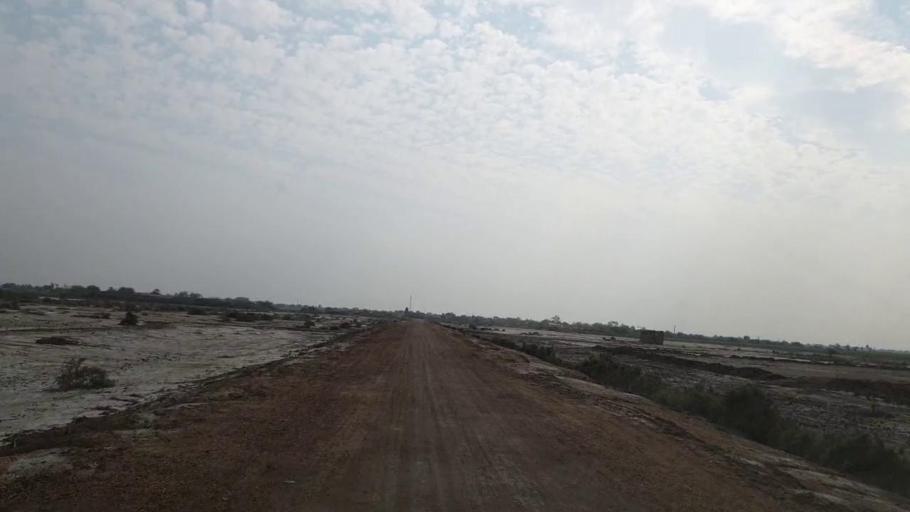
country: PK
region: Sindh
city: Mirpur Khas
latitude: 25.5538
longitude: 69.1596
